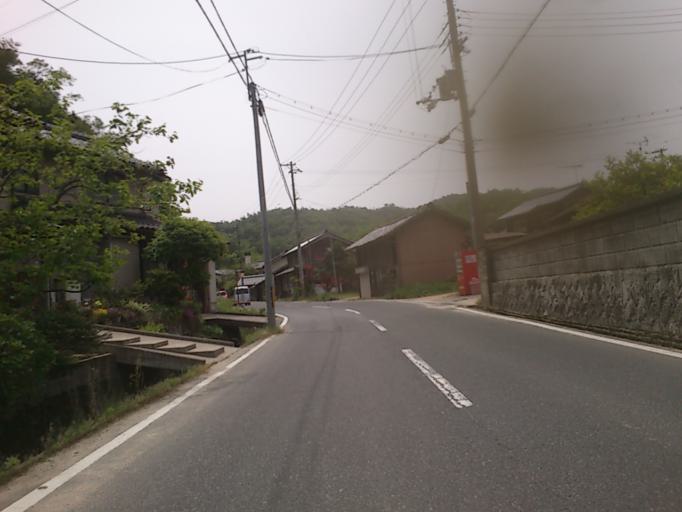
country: JP
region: Kyoto
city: Miyazu
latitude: 35.5991
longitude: 135.0660
